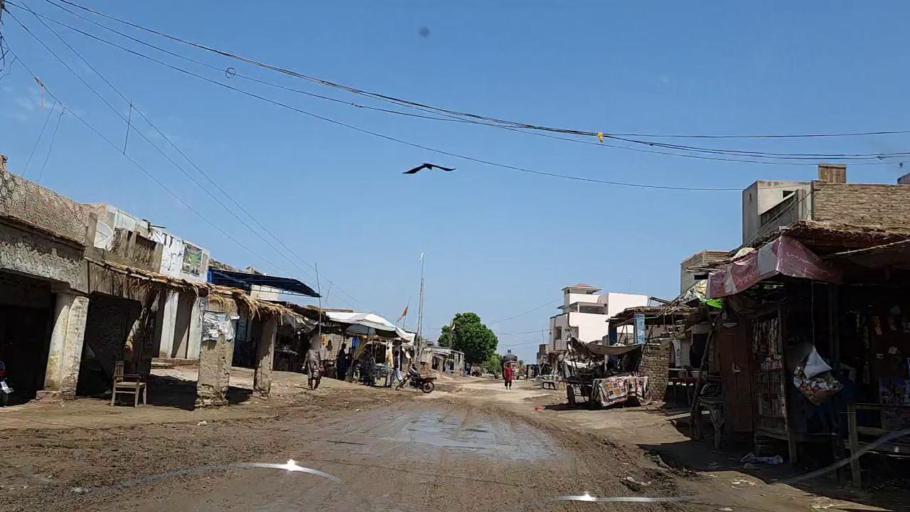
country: PK
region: Sindh
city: Naushahro Firoz
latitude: 26.8105
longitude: 68.1973
